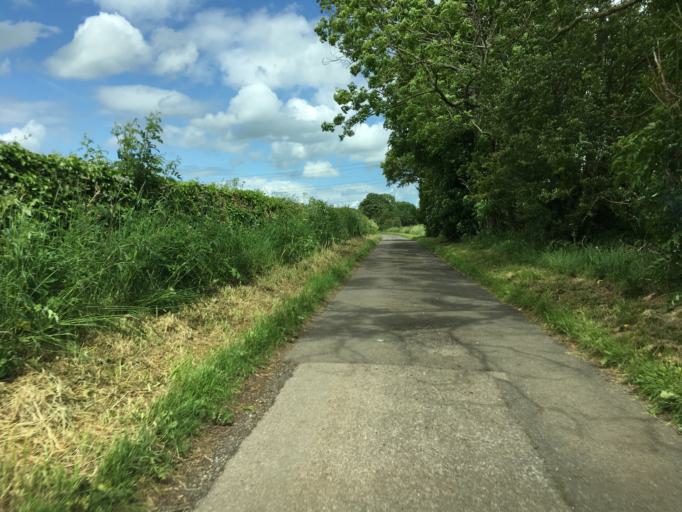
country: GB
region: England
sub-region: Gloucestershire
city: Cirencester
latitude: 51.7621
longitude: -1.9836
